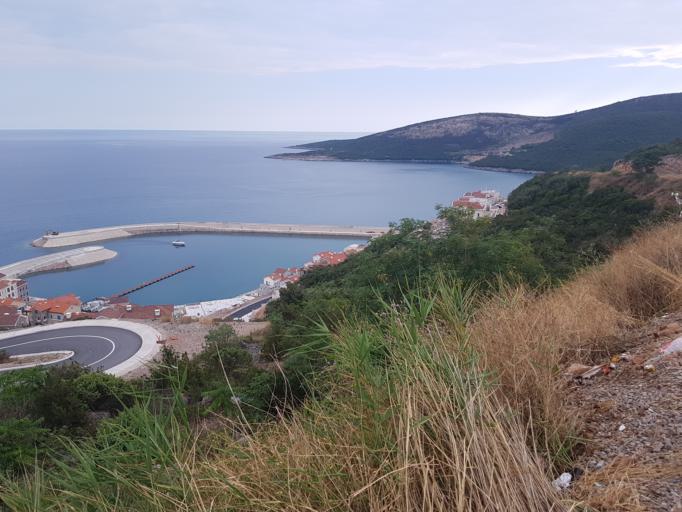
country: ME
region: Tivat
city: Tivat
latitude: 42.3891
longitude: 18.6637
